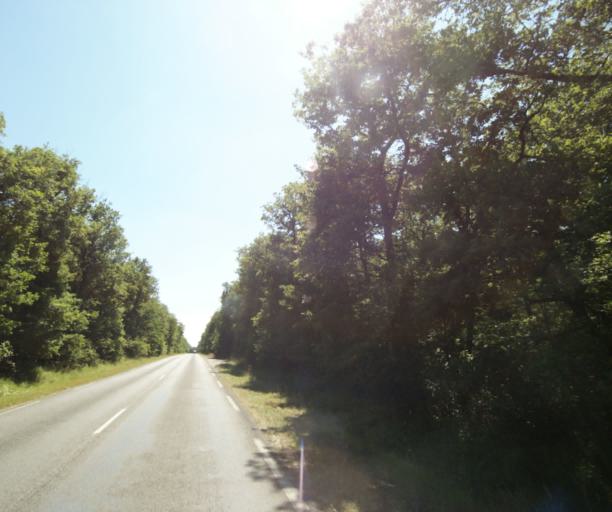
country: FR
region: Centre
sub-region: Departement du Loiret
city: Malesherbes
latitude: 48.3117
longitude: 2.4375
